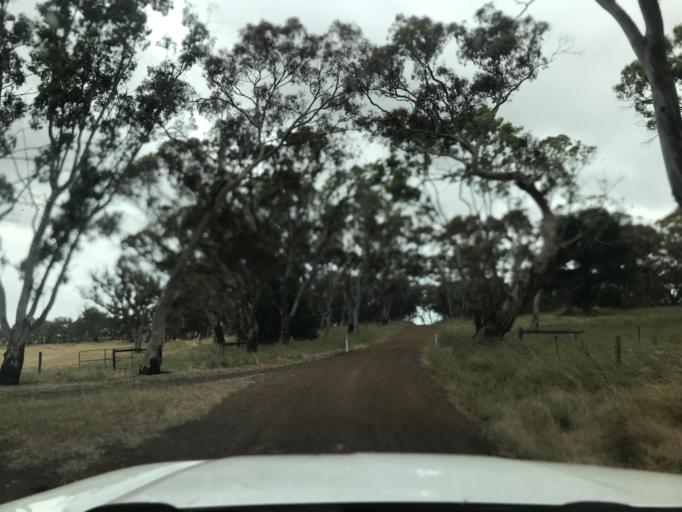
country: AU
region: South Australia
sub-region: Wattle Range
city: Penola
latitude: -37.2345
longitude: 141.4785
